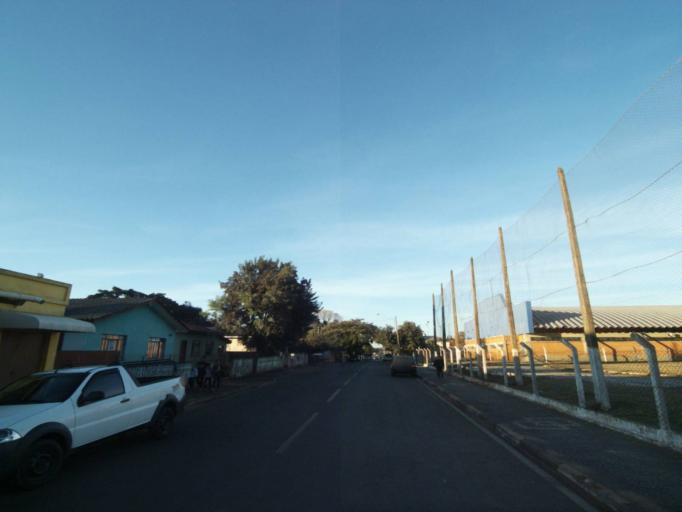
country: BR
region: Parana
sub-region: Tibagi
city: Tibagi
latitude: -24.5127
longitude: -50.4168
